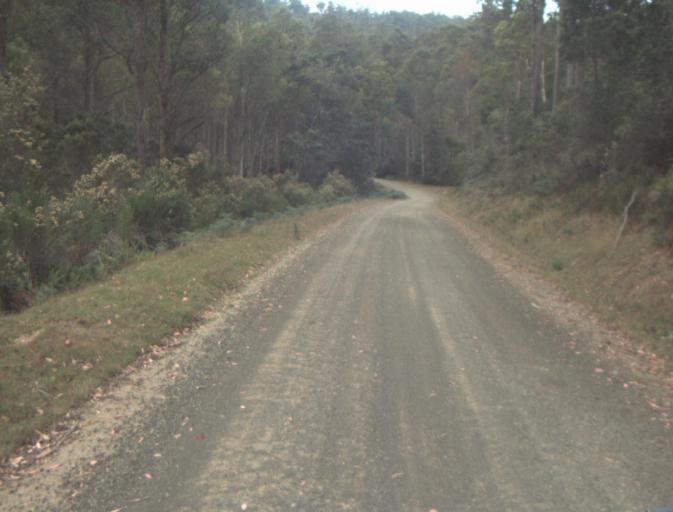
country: AU
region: Tasmania
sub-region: Dorset
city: Scottsdale
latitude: -41.4079
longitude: 147.5193
